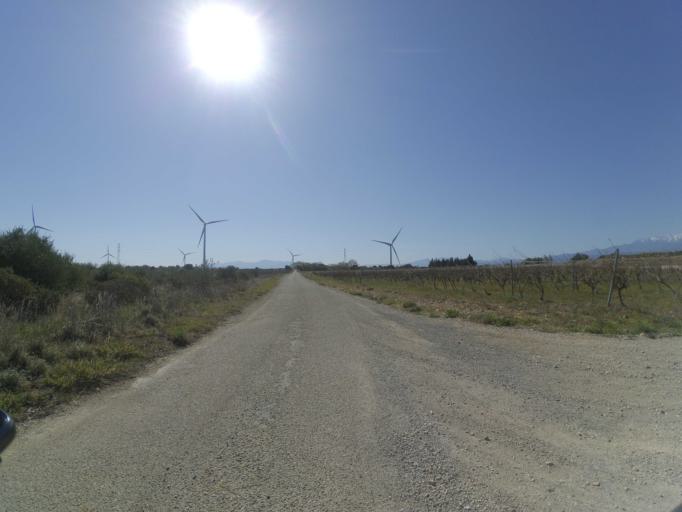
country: FR
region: Languedoc-Roussillon
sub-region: Departement des Pyrenees-Orientales
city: Pezilla-la-Riviere
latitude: 42.7208
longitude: 2.7697
